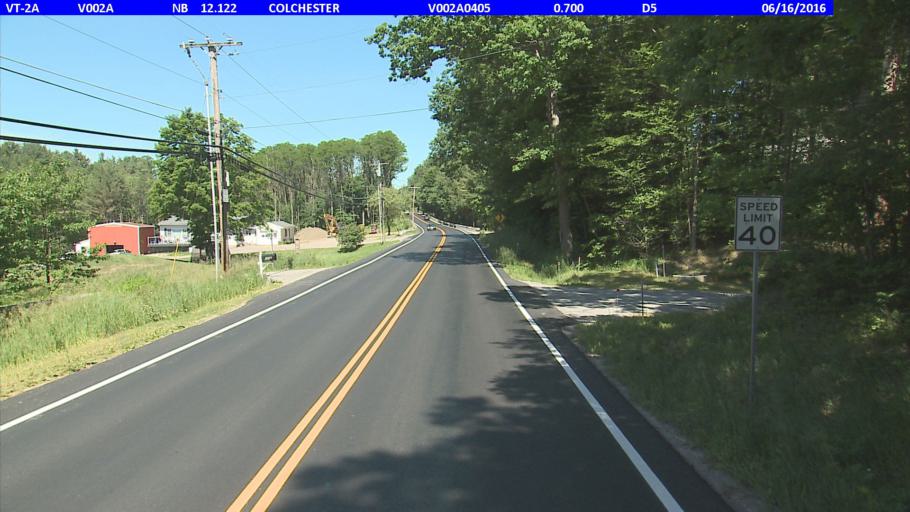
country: US
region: Vermont
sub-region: Chittenden County
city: Colchester
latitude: 44.5365
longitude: -73.1368
